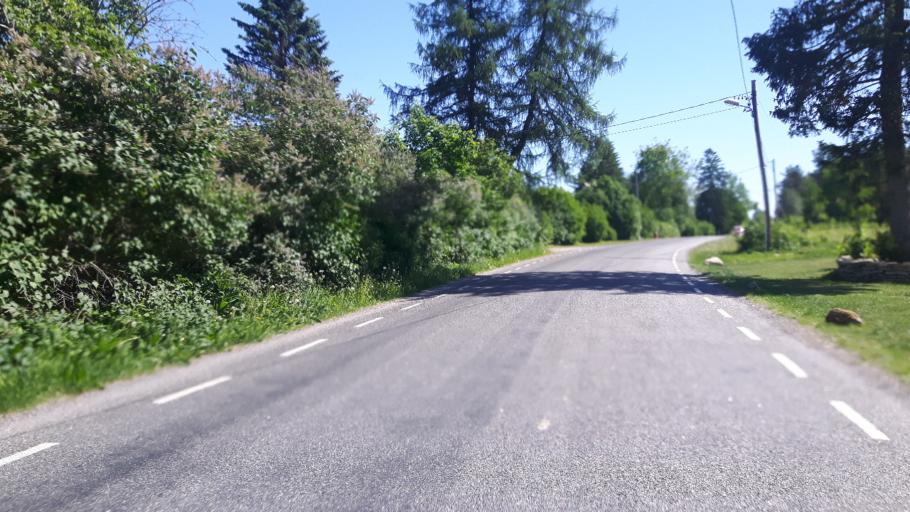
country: EE
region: Raplamaa
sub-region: Kohila vald
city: Kohila
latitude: 59.1753
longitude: 24.7317
